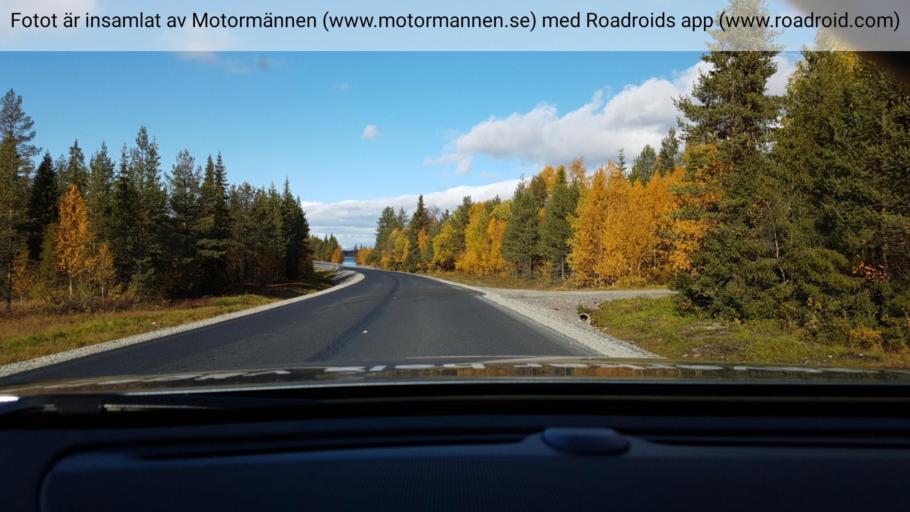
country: SE
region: Norrbotten
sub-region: Arjeplogs Kommun
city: Arjeplog
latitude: 65.9672
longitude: 18.2646
